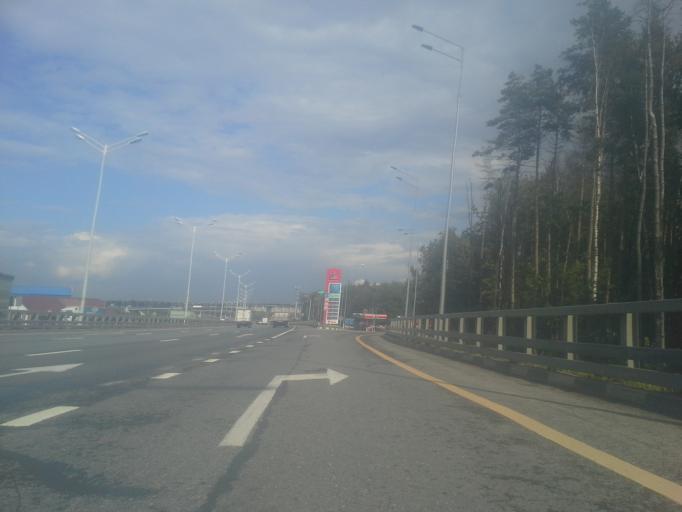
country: RU
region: Moskovskaya
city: Lesnoy Gorodok
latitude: 55.6257
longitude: 37.1903
